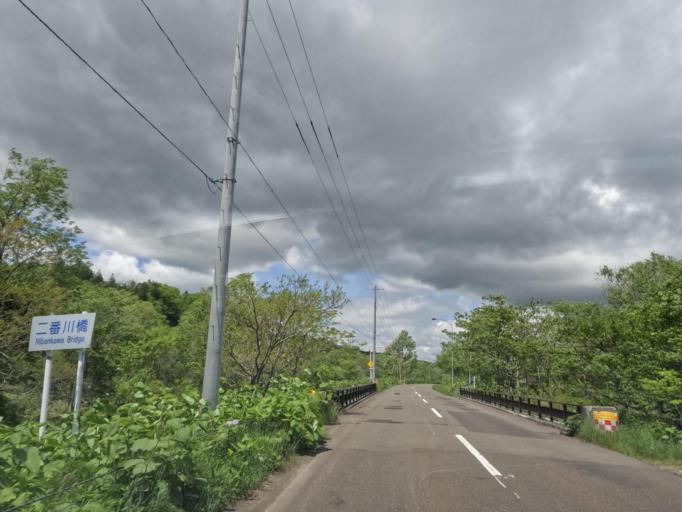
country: JP
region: Hokkaido
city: Tobetsu
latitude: 43.4473
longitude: 141.5843
